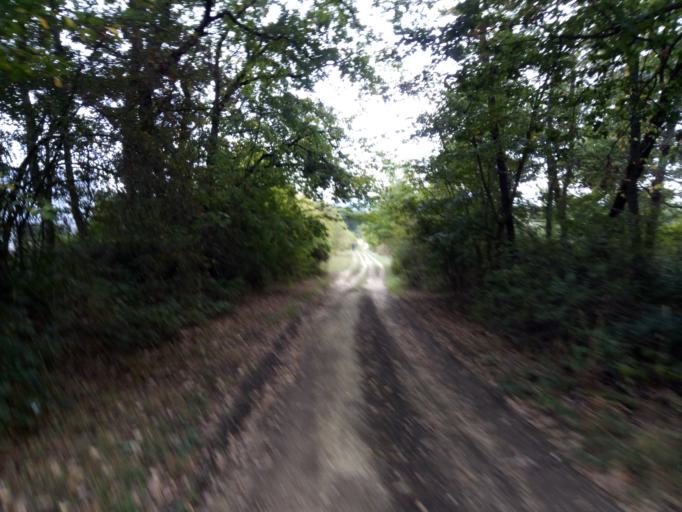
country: DE
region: Rheinland-Pfalz
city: Roth
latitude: 49.9260
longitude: 7.8088
